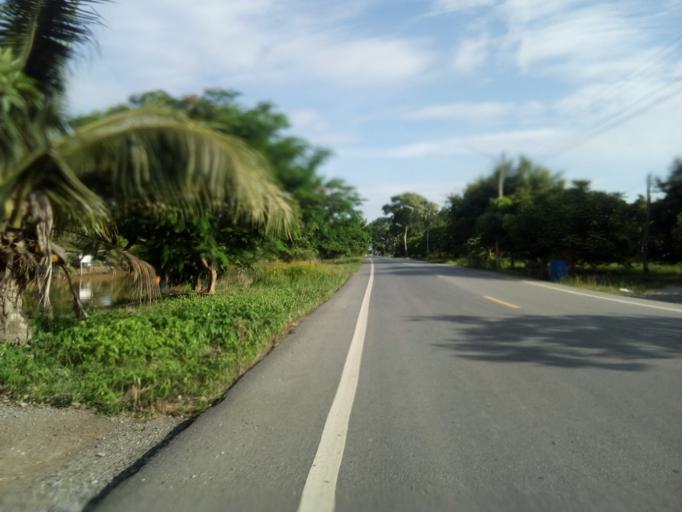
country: TH
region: Pathum Thani
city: Nong Suea
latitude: 14.1082
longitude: 100.8461
